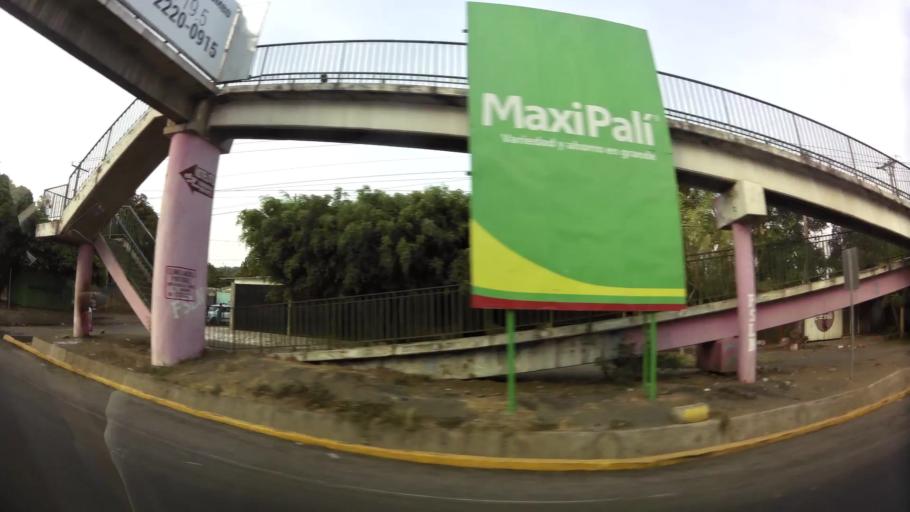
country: NI
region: Managua
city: Ciudad Sandino
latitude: 12.1691
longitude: -86.3428
